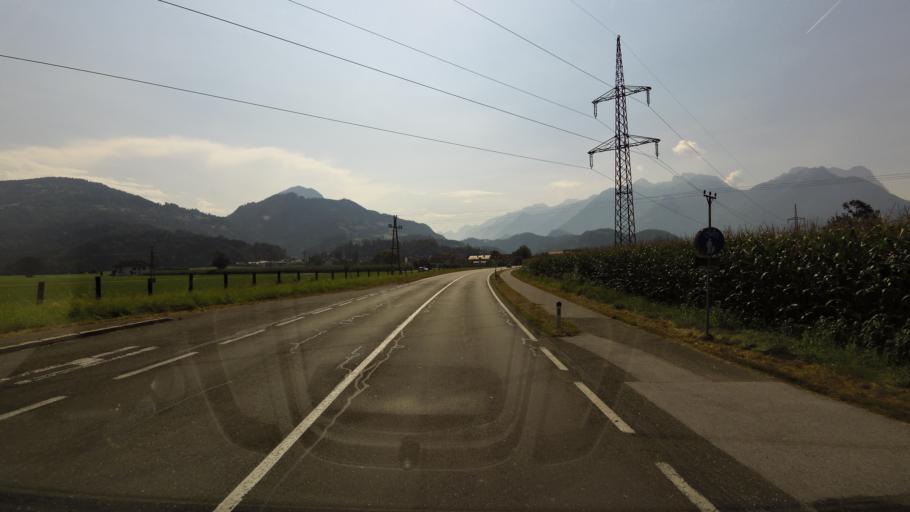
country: AT
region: Salzburg
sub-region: Politischer Bezirk Hallein
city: Kuchl
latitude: 47.6202
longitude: 13.1562
